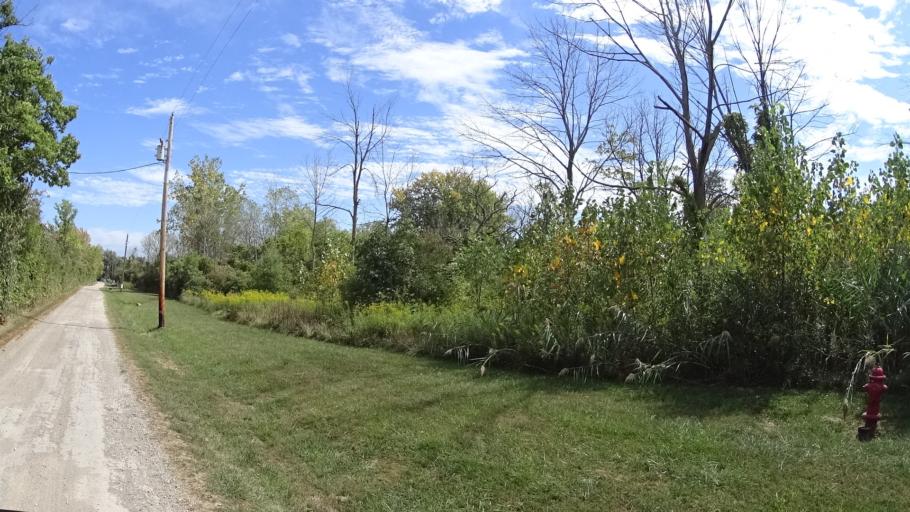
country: US
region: Ohio
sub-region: Erie County
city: Sandusky
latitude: 41.6009
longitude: -82.6836
